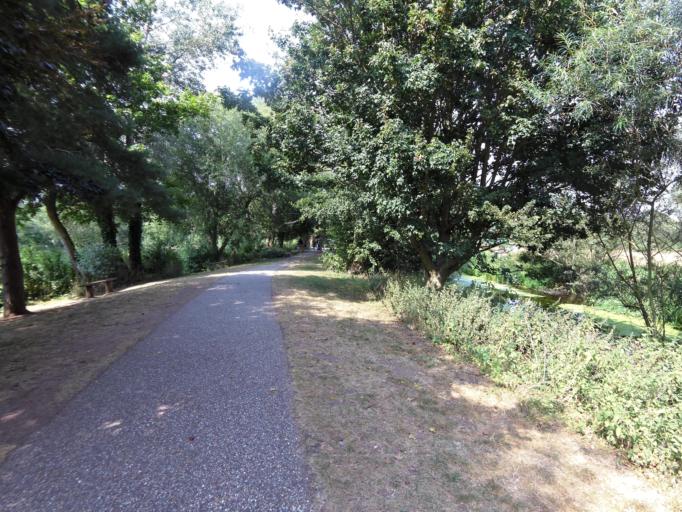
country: GB
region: England
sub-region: Suffolk
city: Needham Market
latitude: 52.1515
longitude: 1.0601
